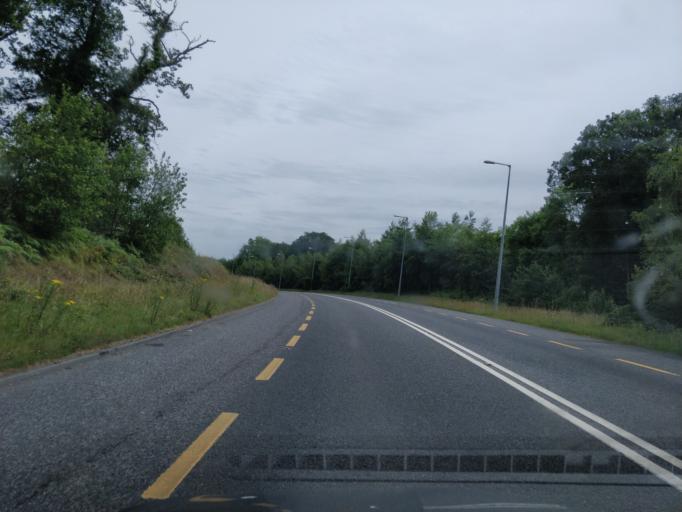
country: IE
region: Leinster
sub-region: Uibh Fhaili
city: Tullamore
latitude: 53.2532
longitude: -7.5194
